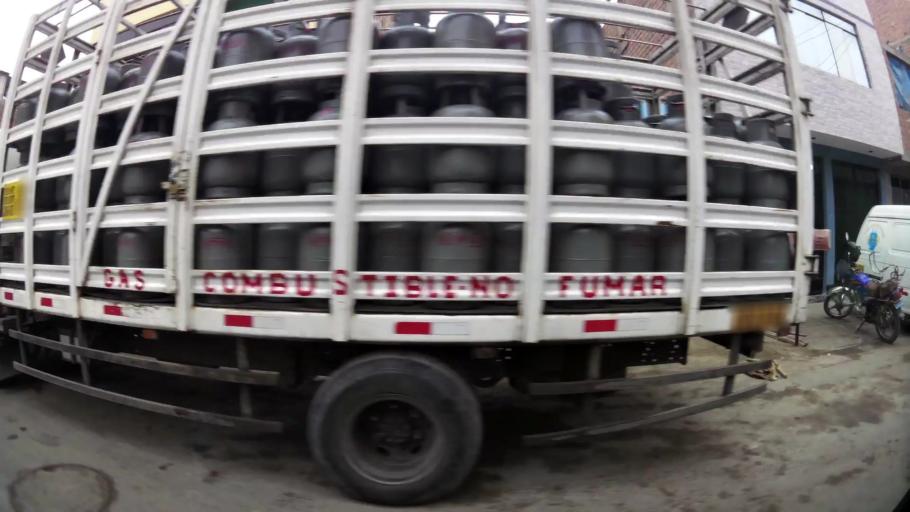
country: PE
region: Lima
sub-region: Lima
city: Independencia
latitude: -11.9682
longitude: -77.0788
